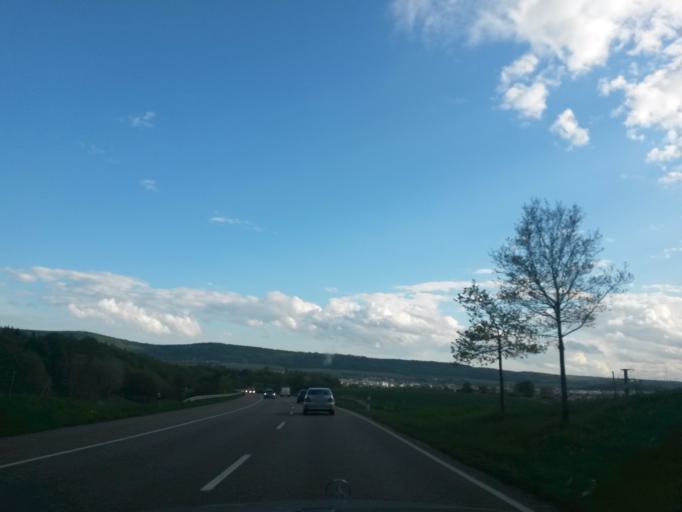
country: DE
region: Baden-Wuerttemberg
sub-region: Regierungsbezirk Stuttgart
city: Aalen
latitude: 48.8525
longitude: 10.0698
